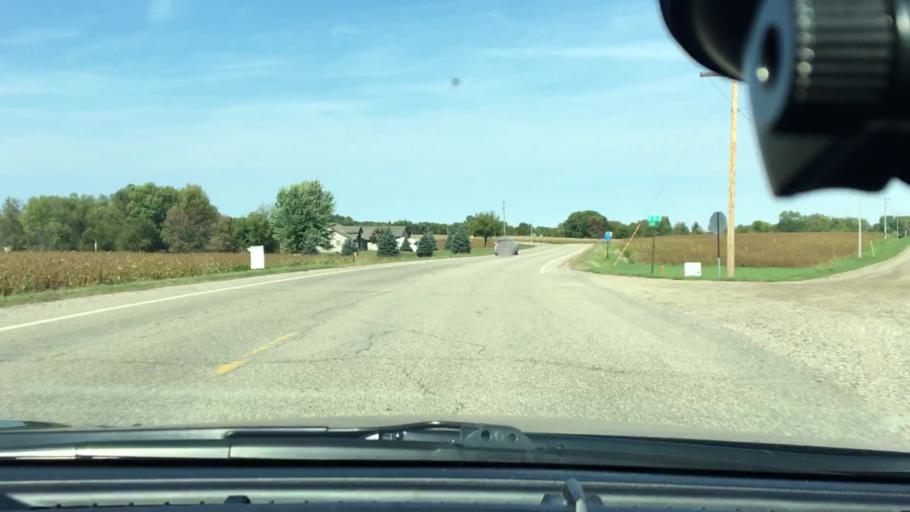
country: US
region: Minnesota
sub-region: Hennepin County
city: Corcoran
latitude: 45.1061
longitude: -93.5639
